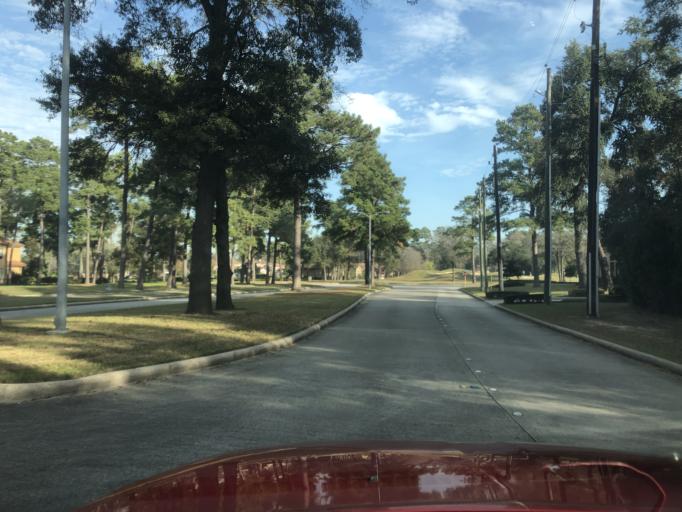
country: US
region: Texas
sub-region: Harris County
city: Spring
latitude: 30.0033
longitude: -95.4764
